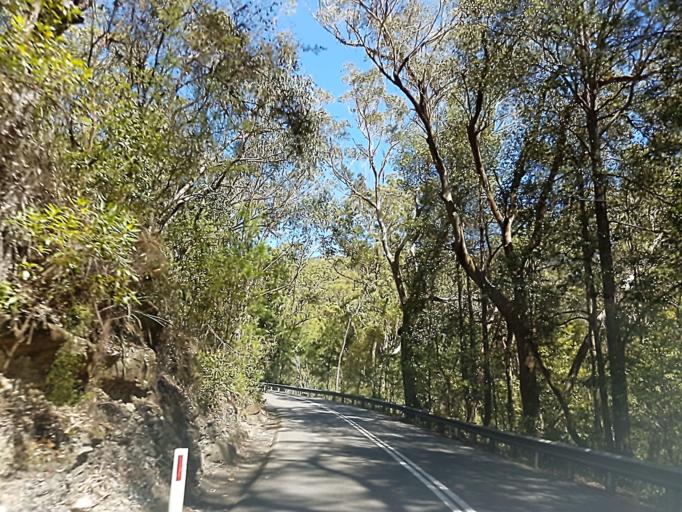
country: AU
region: New South Wales
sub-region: Hornsby Shire
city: Hornsby Heights
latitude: -33.6579
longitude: 151.0777
